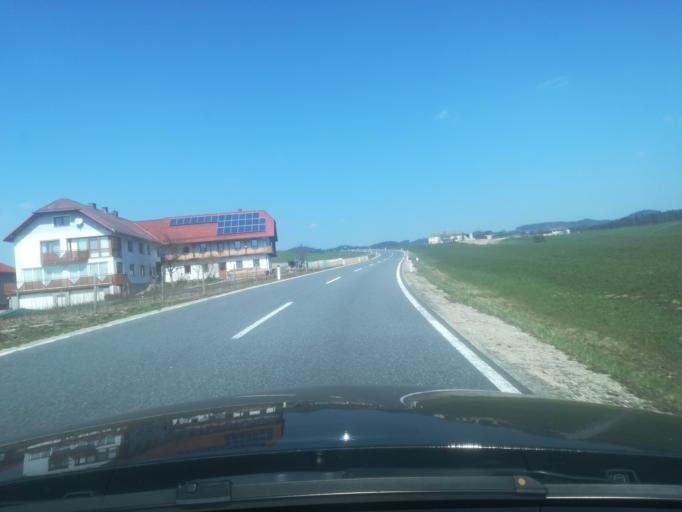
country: AT
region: Upper Austria
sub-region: Politischer Bezirk Perg
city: Perg
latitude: 48.3671
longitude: 14.6819
